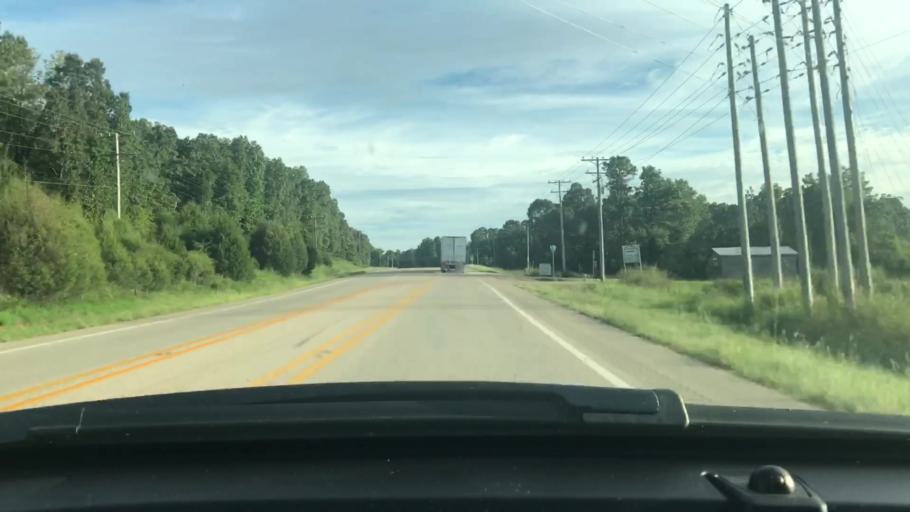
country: US
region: Arkansas
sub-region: Lawrence County
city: Hoxie
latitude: 36.1355
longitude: -91.1583
